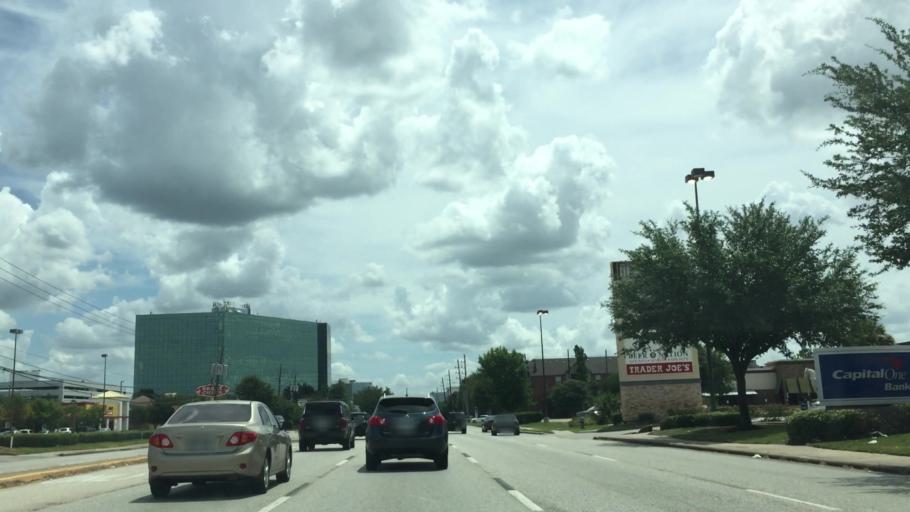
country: US
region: Texas
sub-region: Harris County
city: Bunker Hill Village
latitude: 29.7360
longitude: -95.5839
